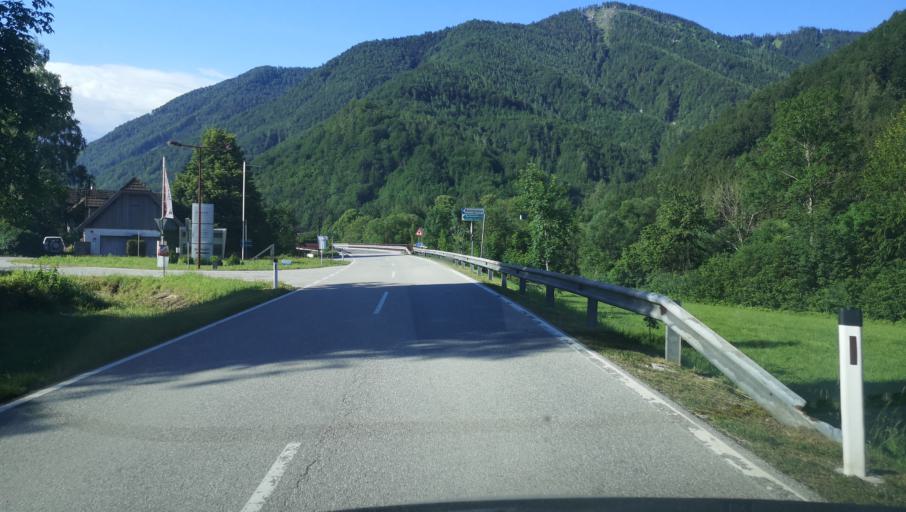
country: AT
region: Lower Austria
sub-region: Politischer Bezirk Amstetten
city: Hollenstein an der Ybbs
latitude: 47.8294
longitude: 14.7525
